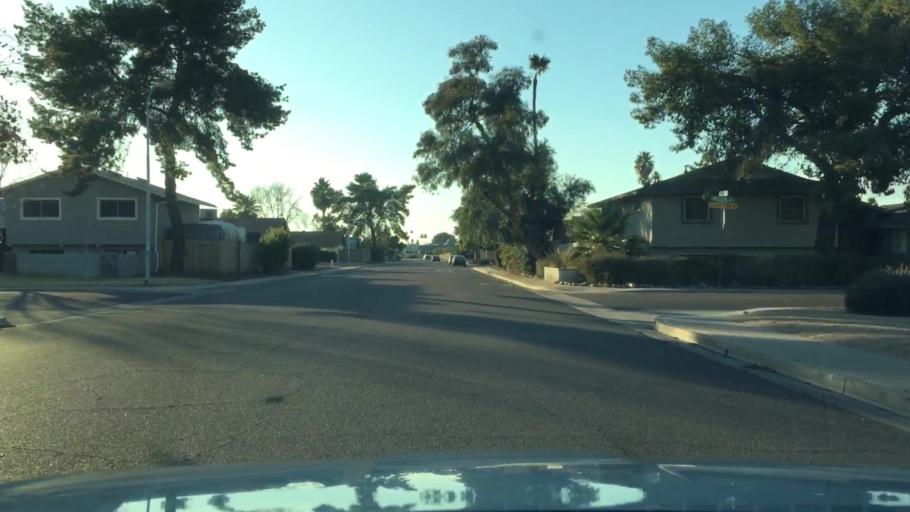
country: US
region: Arizona
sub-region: Maricopa County
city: Tempe
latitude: 33.3839
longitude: -111.9116
